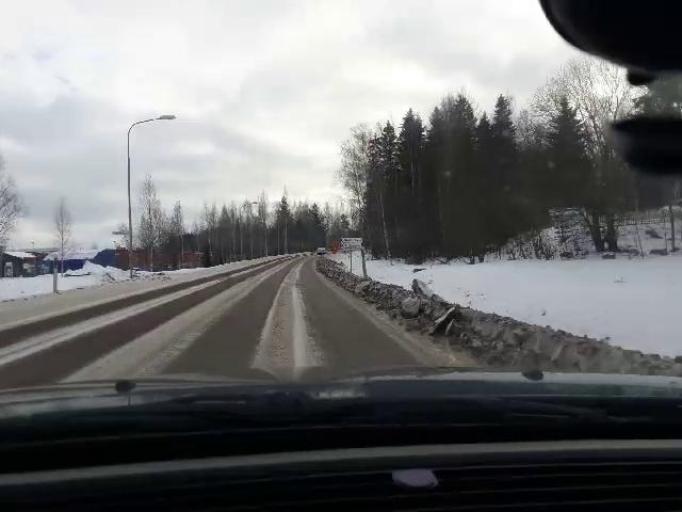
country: SE
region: Gaevleborg
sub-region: Bollnas Kommun
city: Bollnas
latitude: 61.3374
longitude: 16.3909
